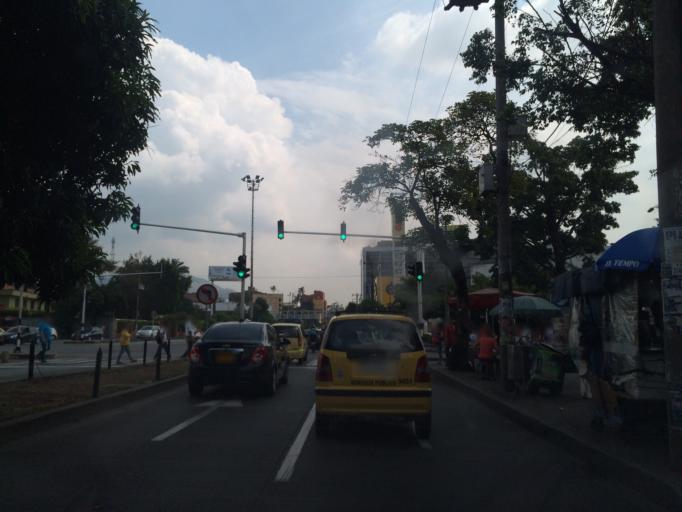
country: CO
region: Valle del Cauca
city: Cali
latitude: 3.4240
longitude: -76.5467
